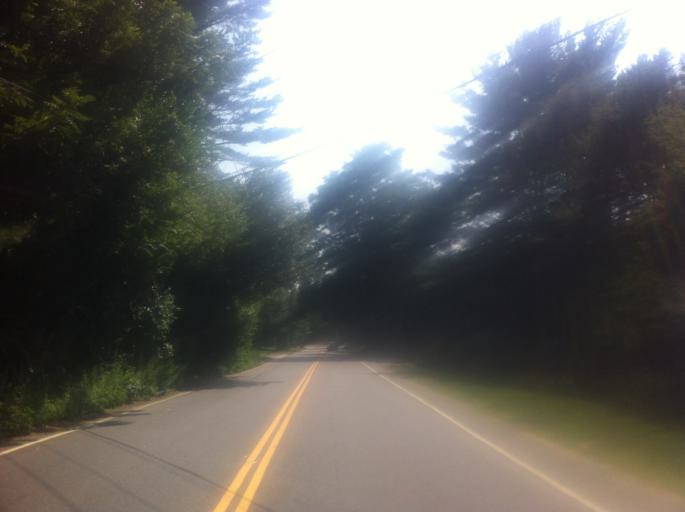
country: US
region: New York
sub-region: Nassau County
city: Brookville
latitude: 40.8196
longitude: -73.5711
